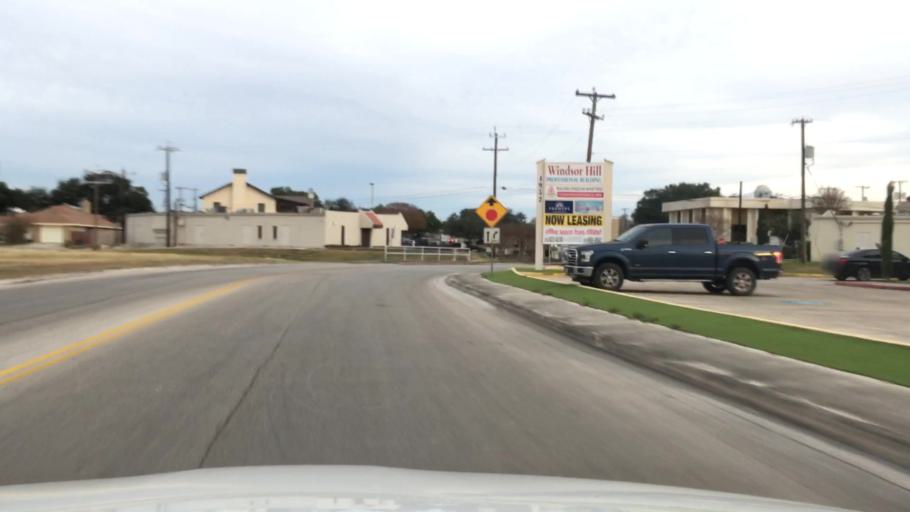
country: US
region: Texas
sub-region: Bexar County
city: Windcrest
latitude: 29.5117
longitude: -98.3910
